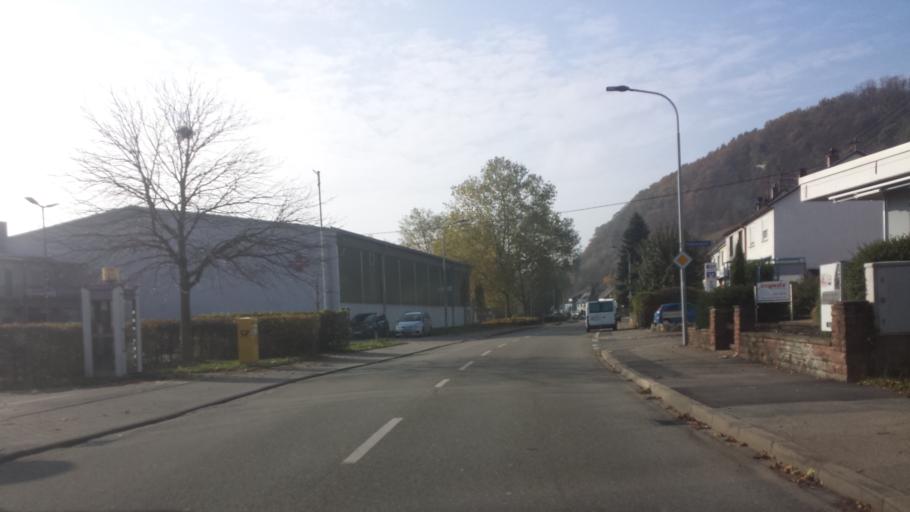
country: DE
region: Baden-Wuerttemberg
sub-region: Karlsruhe Region
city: Mosbach
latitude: 49.3496
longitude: 9.1314
